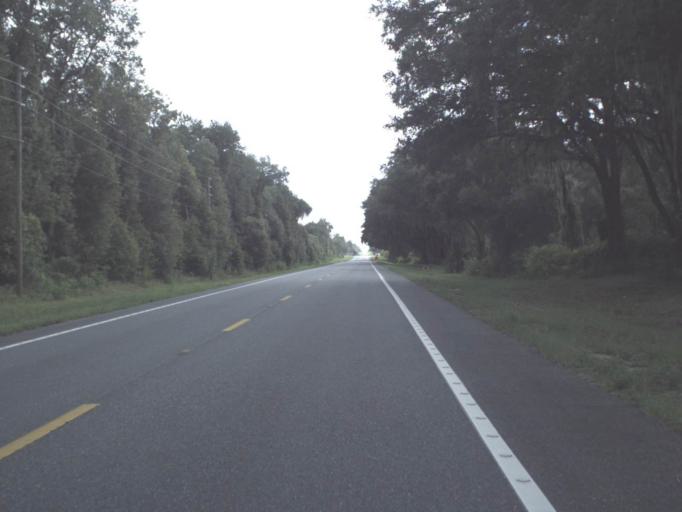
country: US
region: Florida
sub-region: Levy County
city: Williston Highlands
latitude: 29.2824
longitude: -82.5386
